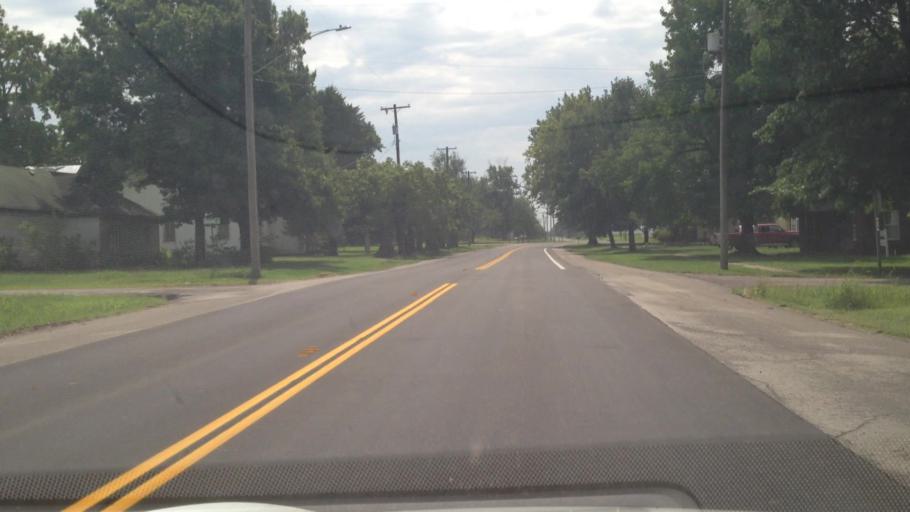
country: US
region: Kansas
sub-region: Crawford County
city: Girard
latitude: 37.6615
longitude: -94.9696
